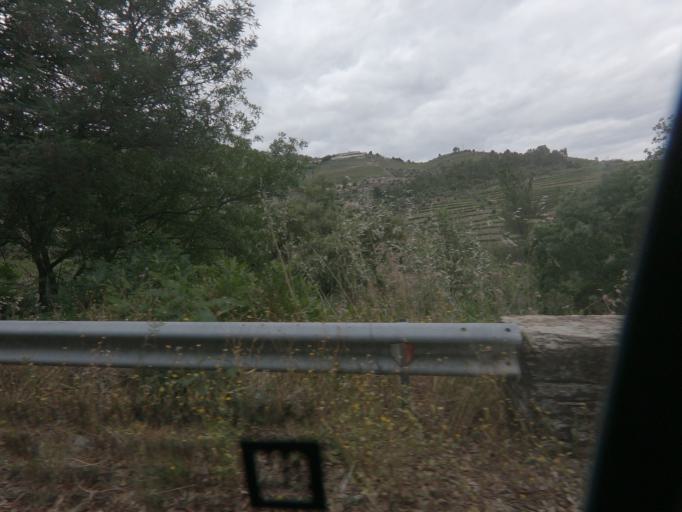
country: PT
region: Vila Real
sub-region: Sabrosa
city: Vilela
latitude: 41.2003
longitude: -7.5601
